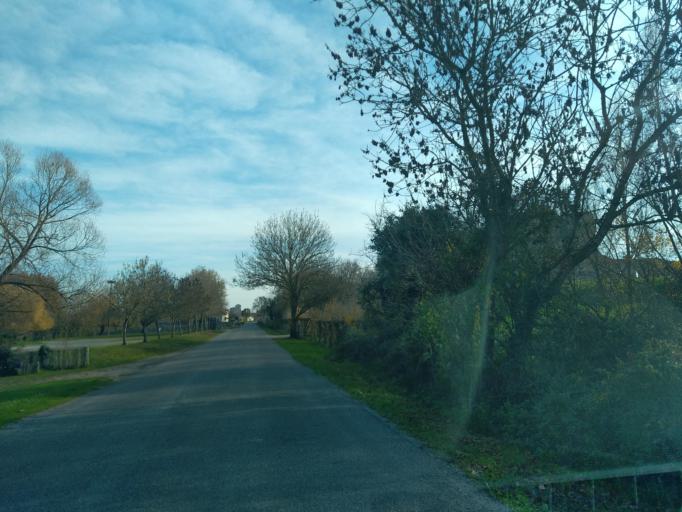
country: FR
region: Pays de la Loire
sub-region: Departement de la Vendee
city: Maillezais
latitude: 46.3746
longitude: -0.7482
